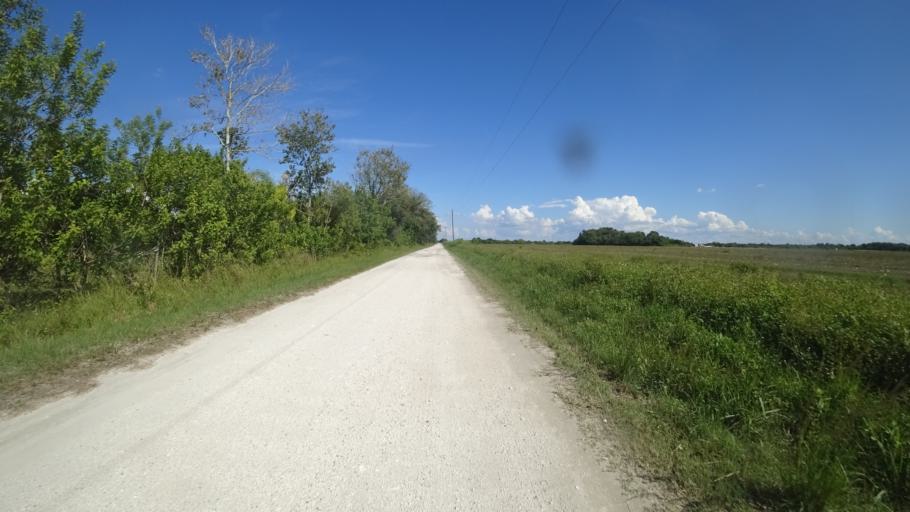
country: US
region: Florida
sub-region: Sarasota County
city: The Meadows
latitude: 27.4450
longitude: -82.2756
